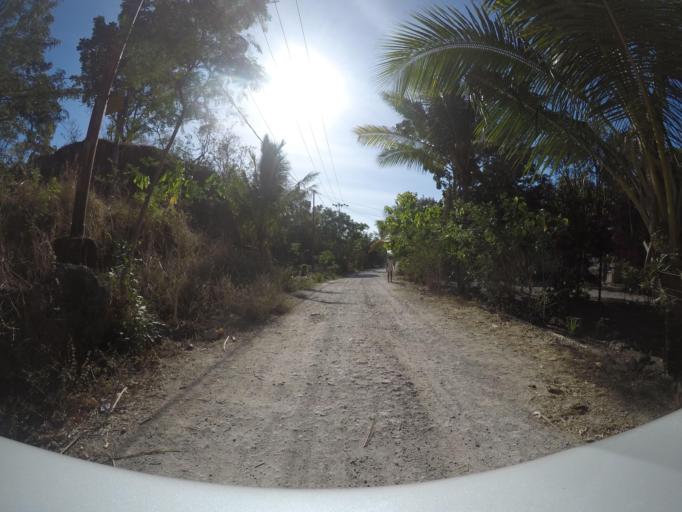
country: TL
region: Baucau
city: Baucau
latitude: -8.4508
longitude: 126.4319
